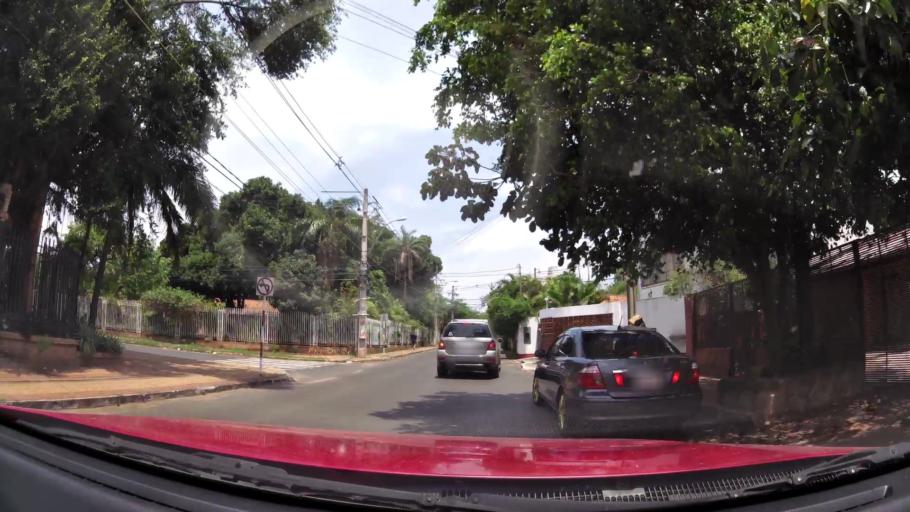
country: PY
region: Central
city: Fernando de la Mora
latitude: -25.3044
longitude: -57.5642
